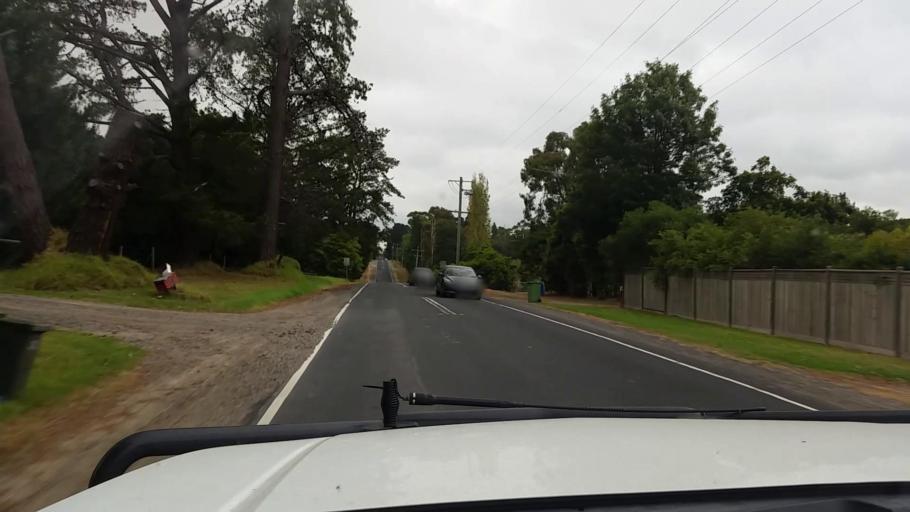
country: AU
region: Victoria
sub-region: Mornington Peninsula
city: Hastings
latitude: -38.2907
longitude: 145.1456
